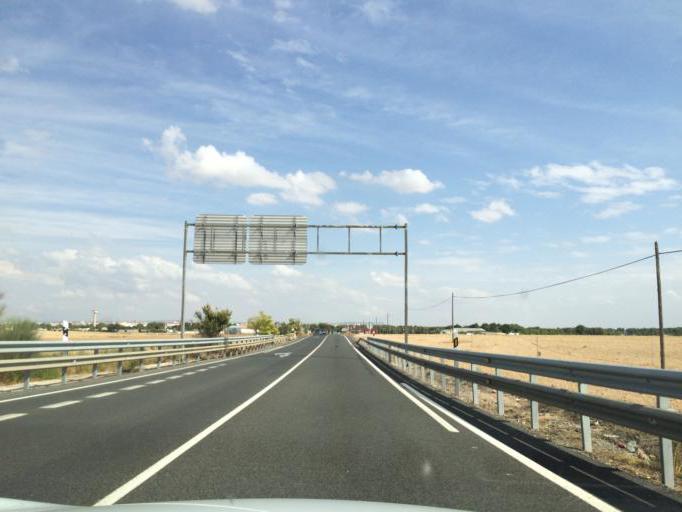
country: ES
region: Castille-La Mancha
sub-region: Provincia de Albacete
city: Albacete
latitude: 39.0004
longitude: -1.9003
